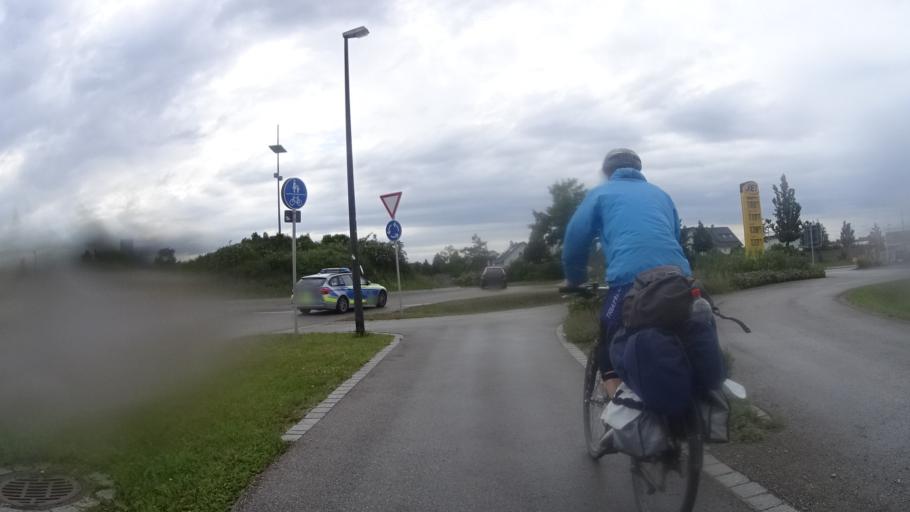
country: DE
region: Bavaria
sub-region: Upper Bavaria
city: Maisach
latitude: 48.2162
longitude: 11.2706
